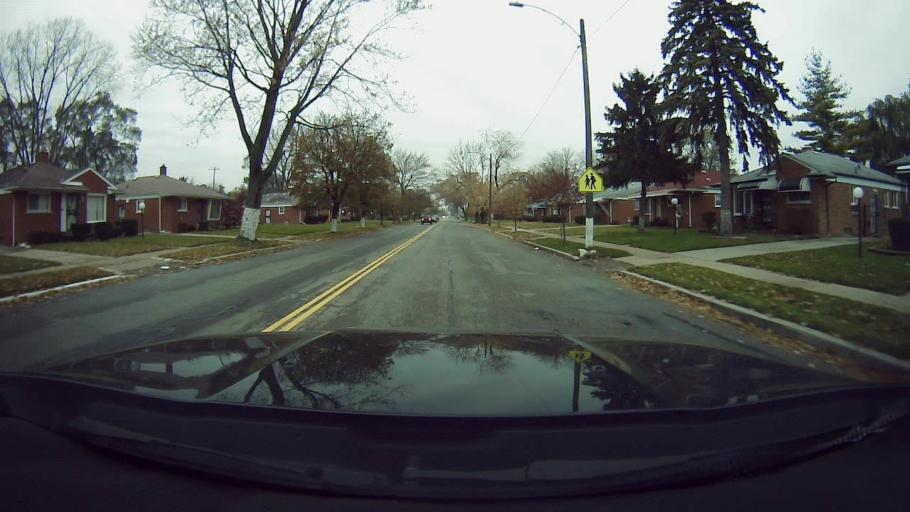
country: US
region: Michigan
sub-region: Wayne County
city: Highland Park
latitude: 42.4271
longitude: -83.0826
